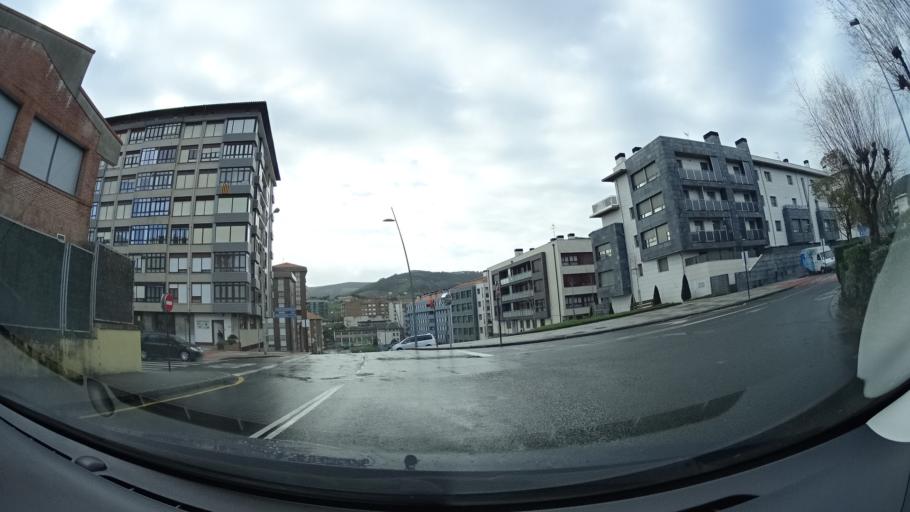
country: ES
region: Basque Country
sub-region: Bizkaia
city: Bermeo
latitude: 43.4220
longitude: -2.7287
